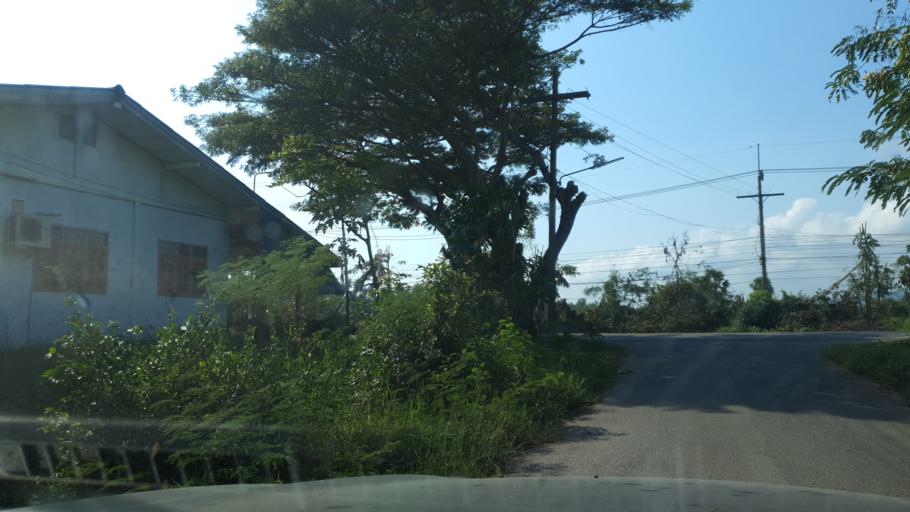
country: TH
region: Prachuap Khiri Khan
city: Thap Sakae
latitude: 11.3615
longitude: 99.5528
